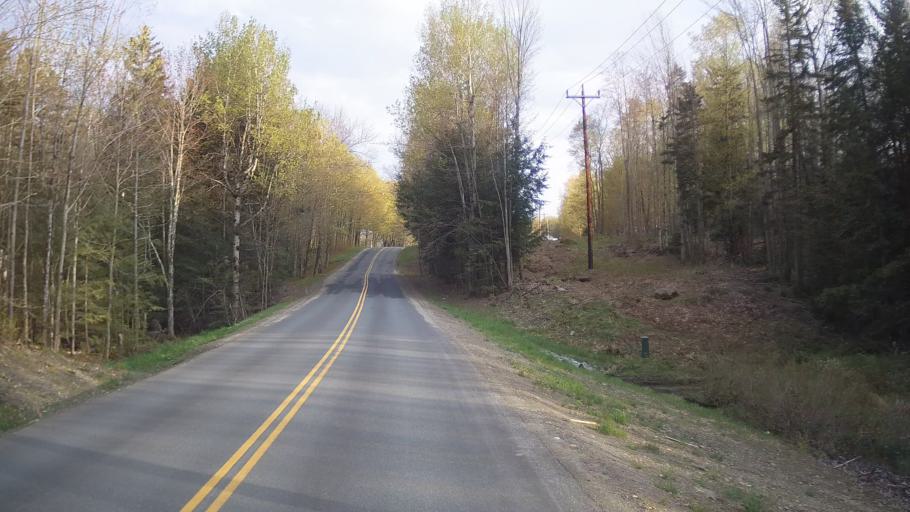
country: US
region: Vermont
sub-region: Orleans County
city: Newport
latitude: 44.9238
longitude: -72.4325
